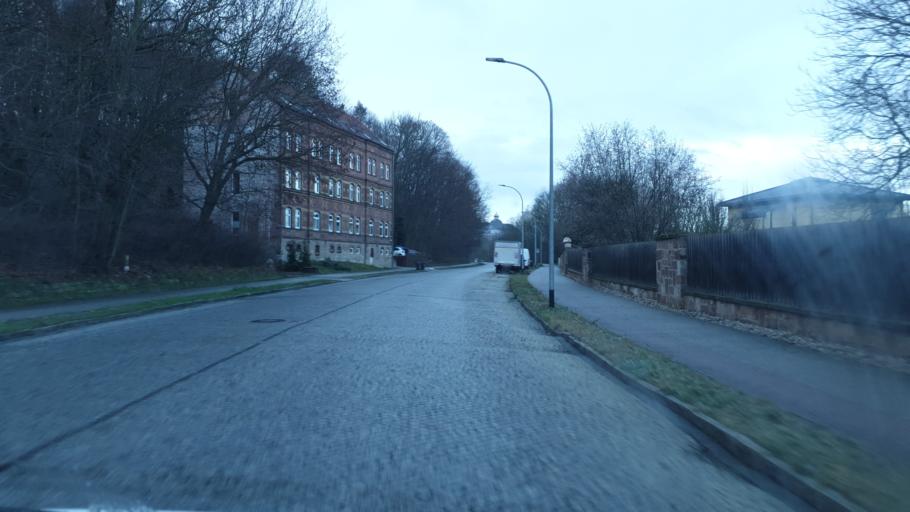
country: DE
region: Saxony-Anhalt
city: Burgwerben
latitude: 51.2079
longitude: 11.9825
